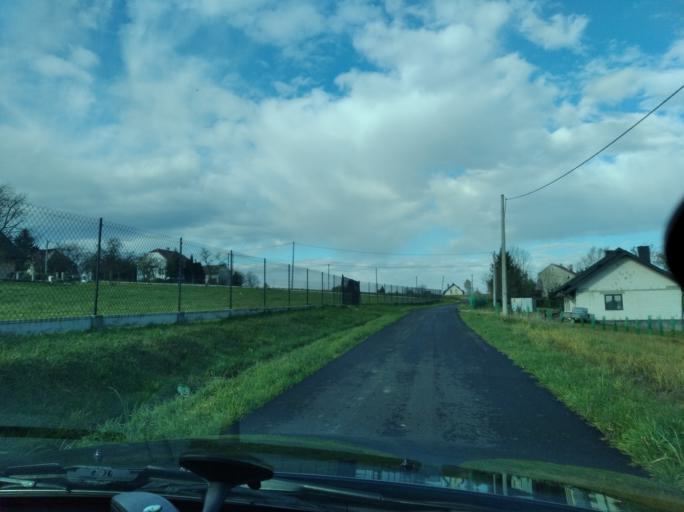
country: PL
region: Subcarpathian Voivodeship
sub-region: Powiat debicki
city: Debica
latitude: 50.0264
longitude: 21.4657
